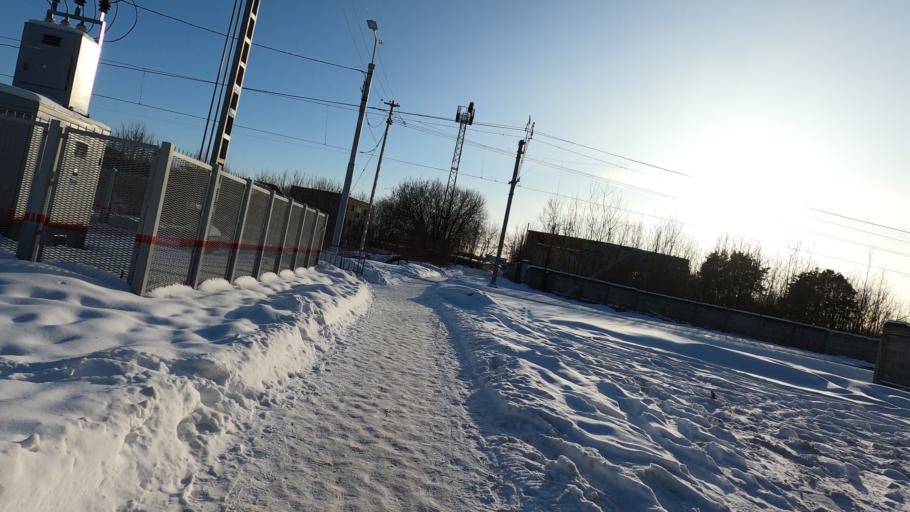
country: RU
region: Moskovskaya
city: Pavlovskiy Posad
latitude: 55.7744
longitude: 38.6975
